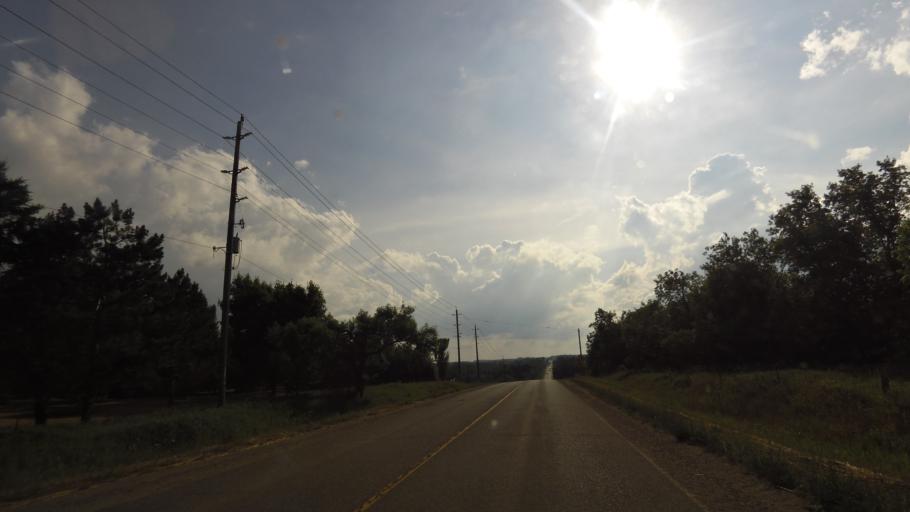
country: CA
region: Ontario
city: Orangeville
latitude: 43.9500
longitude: -80.0868
